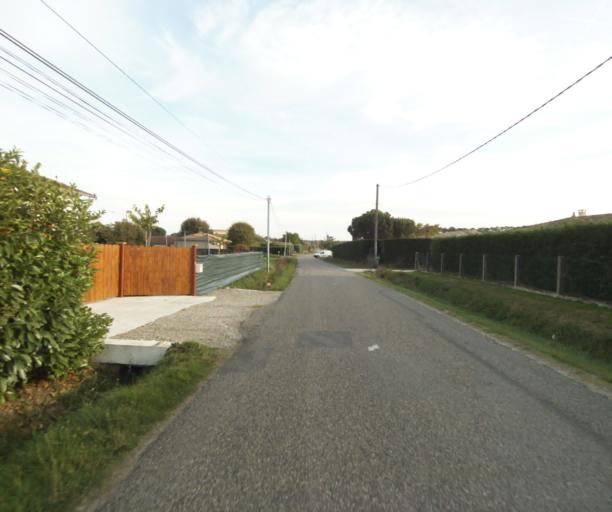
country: FR
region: Midi-Pyrenees
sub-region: Departement du Tarn-et-Garonne
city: Campsas
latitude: 43.8830
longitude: 1.3363
